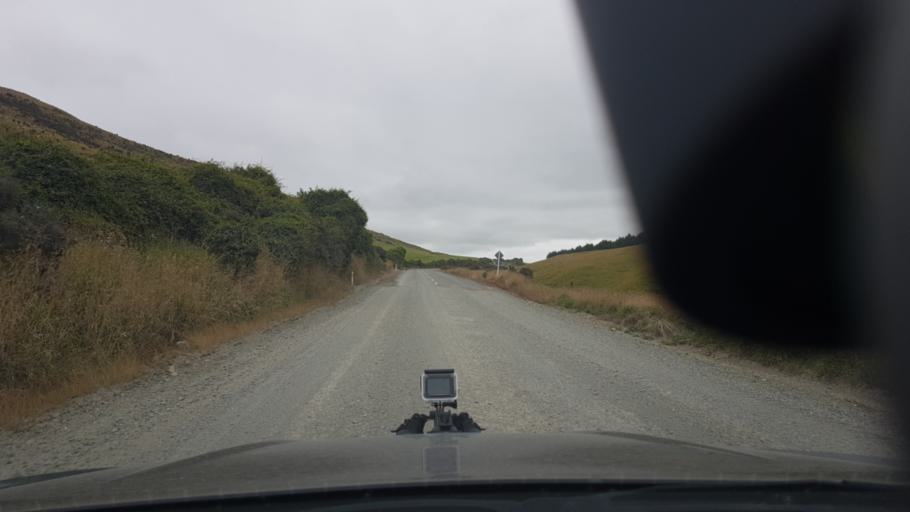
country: NZ
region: Otago
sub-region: Clutha District
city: Papatowai
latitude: -46.3317
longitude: 169.4045
